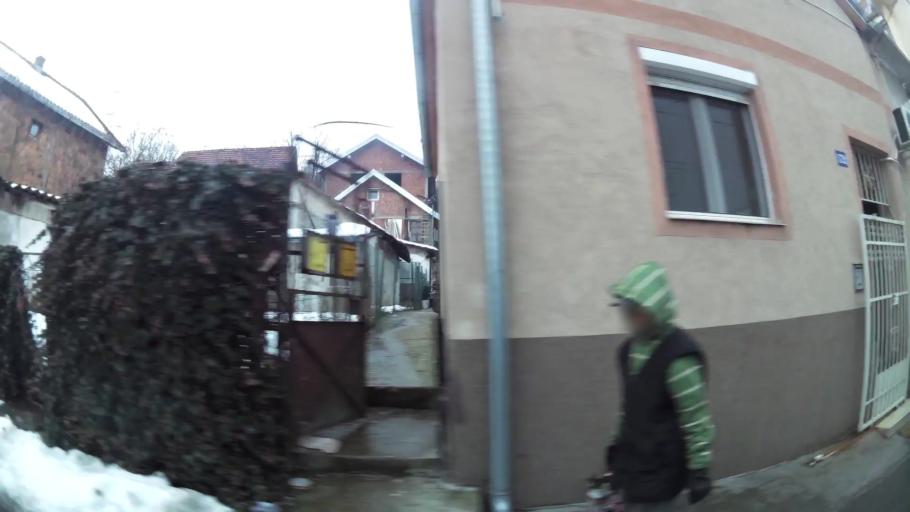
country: RS
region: Central Serbia
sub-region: Belgrade
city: Zvezdara
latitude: 44.7754
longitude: 20.5085
